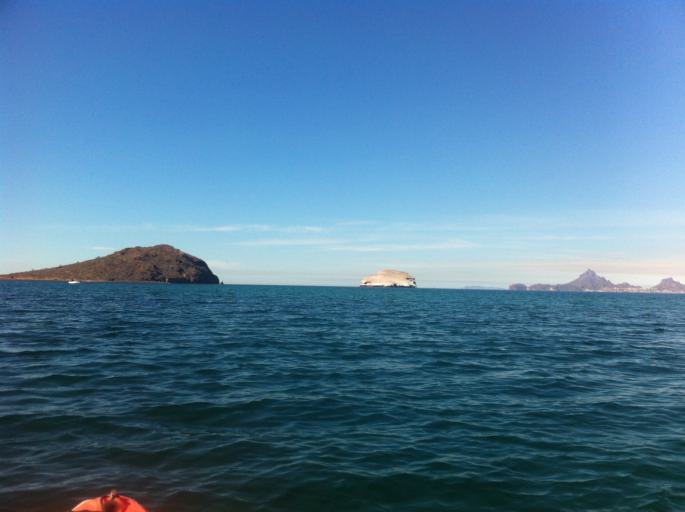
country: MX
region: Sonora
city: Heroica Guaymas
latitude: 27.9089
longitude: -110.9560
